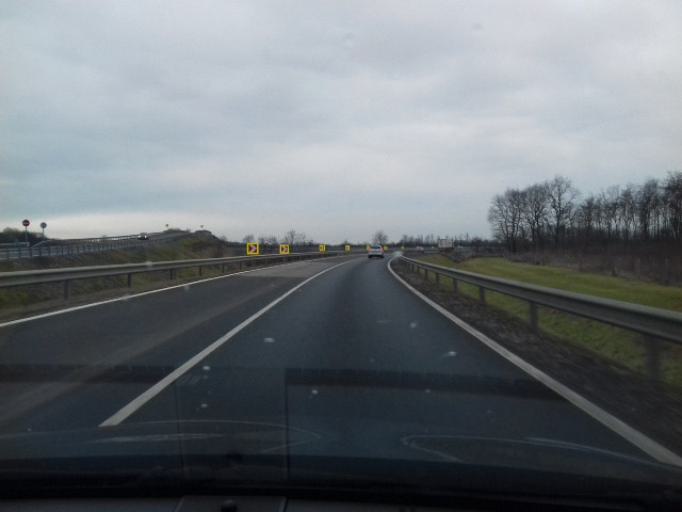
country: HU
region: Szabolcs-Szatmar-Bereg
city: Nagykallo
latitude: 47.9004
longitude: 21.8171
